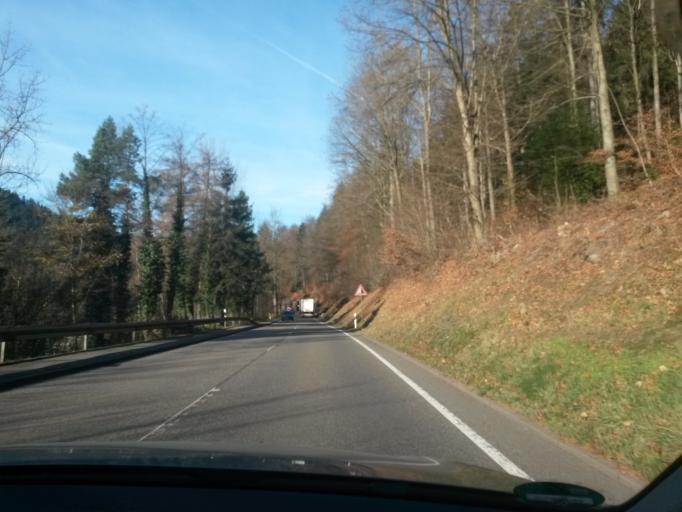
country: DE
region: Baden-Wuerttemberg
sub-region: Karlsruhe Region
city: Hofen an der Enz
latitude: 48.8103
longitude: 8.5841
